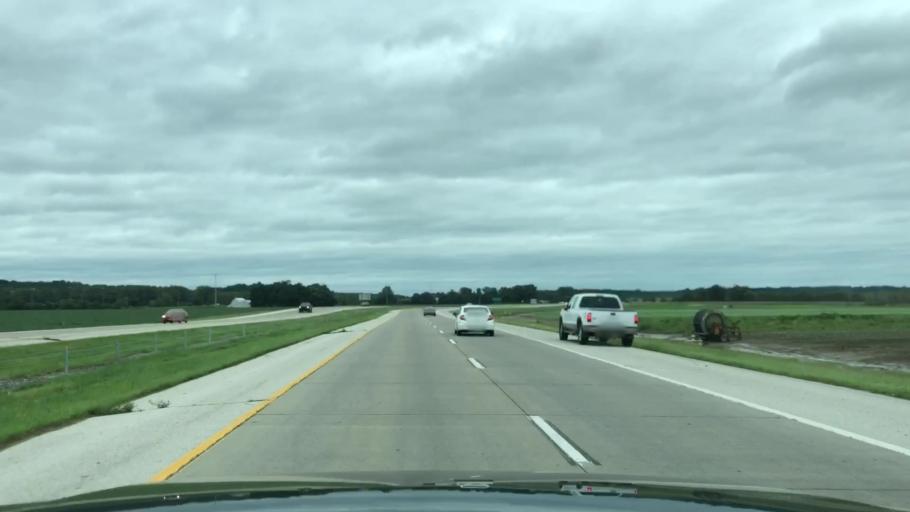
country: US
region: Missouri
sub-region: Saint Charles County
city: Saint Charles
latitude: 38.7229
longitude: -90.4985
